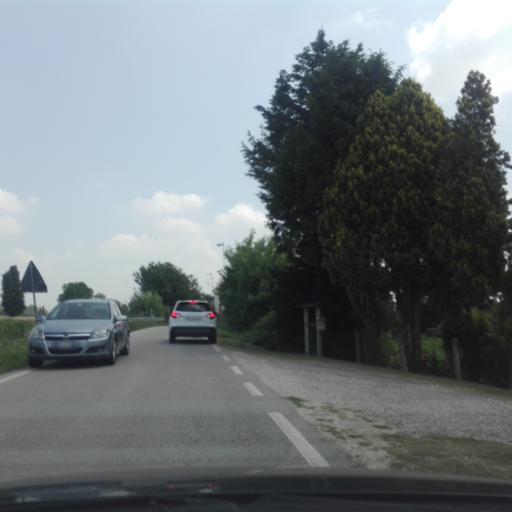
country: IT
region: Veneto
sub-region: Provincia di Rovigo
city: Gavello
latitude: 45.0267
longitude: 11.9478
